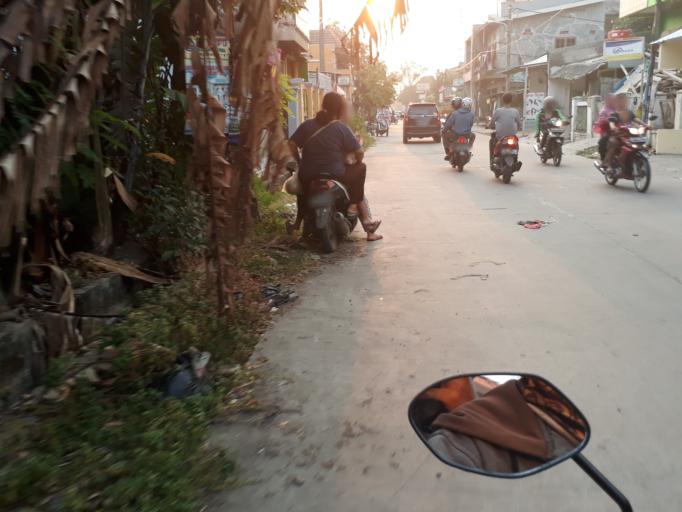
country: ID
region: West Java
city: Bekasi
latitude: -6.2410
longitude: 107.0392
